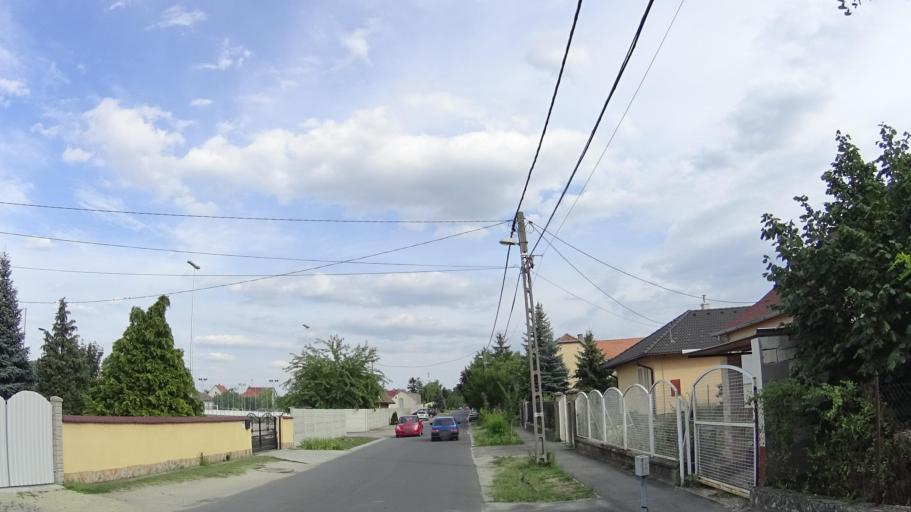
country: HU
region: Pest
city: Dunavarsany
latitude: 47.2741
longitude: 19.0686
